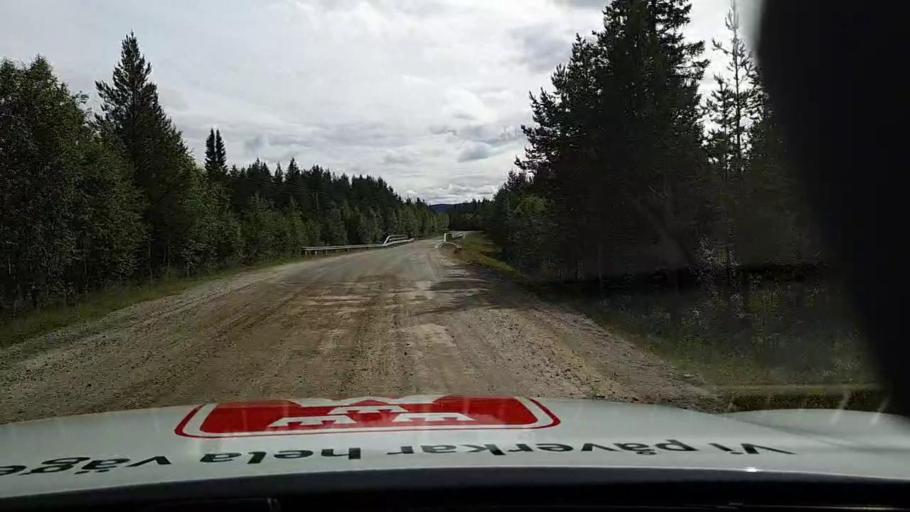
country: SE
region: Jaemtland
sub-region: Are Kommun
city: Jarpen
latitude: 62.5241
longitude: 13.4888
